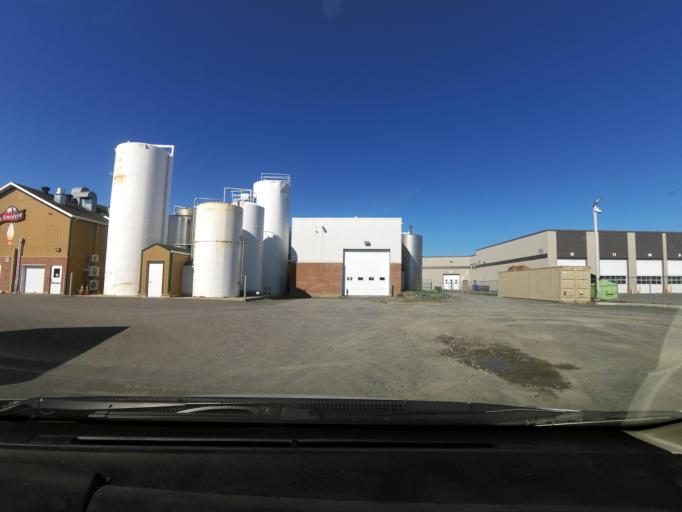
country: CA
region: Quebec
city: Sainte-Catherine
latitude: 46.2921
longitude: -72.5394
